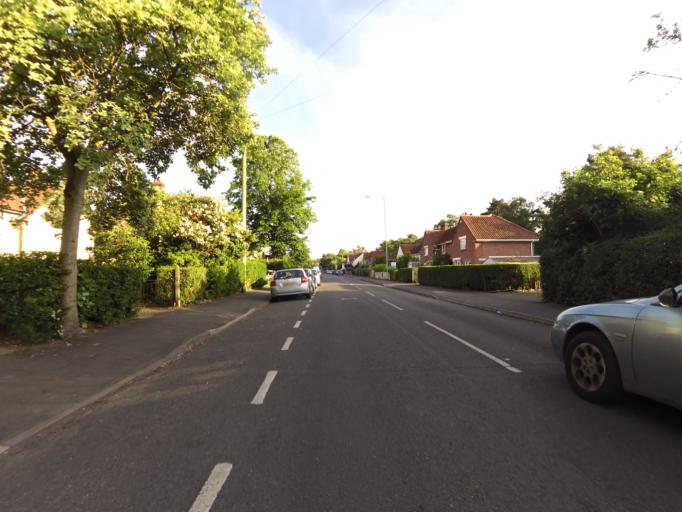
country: GB
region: England
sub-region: Norfolk
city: Norwich
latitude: 52.6476
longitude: 1.2910
